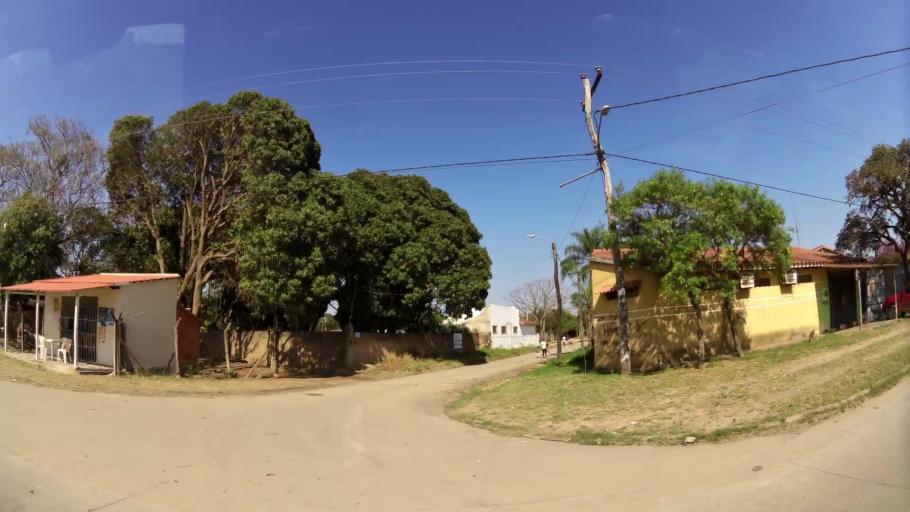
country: BO
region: Santa Cruz
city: Santa Cruz de la Sierra
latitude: -17.7625
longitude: -63.1111
